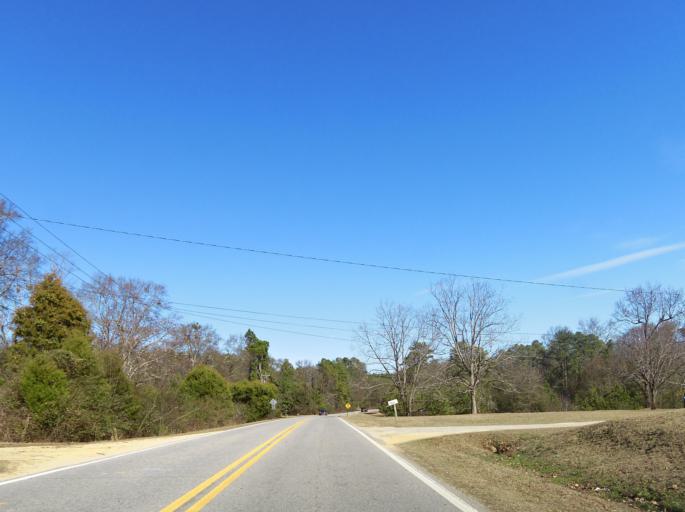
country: US
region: Georgia
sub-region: Peach County
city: Byron
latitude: 32.7330
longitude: -83.7222
